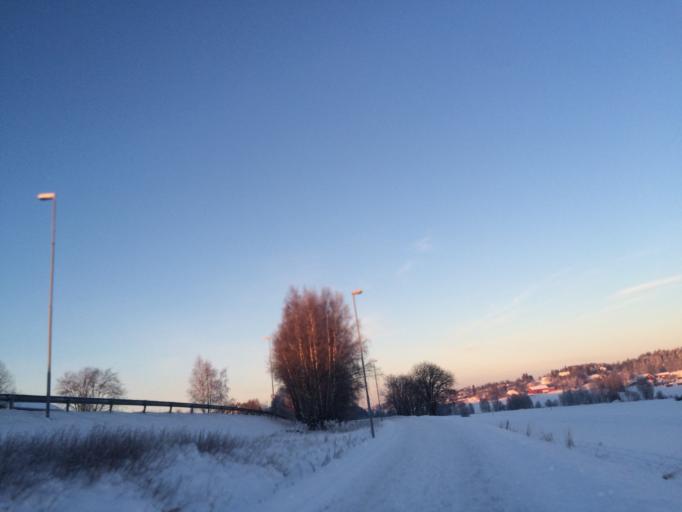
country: NO
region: Akershus
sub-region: Ski
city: Ski
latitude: 59.6965
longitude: 10.8324
